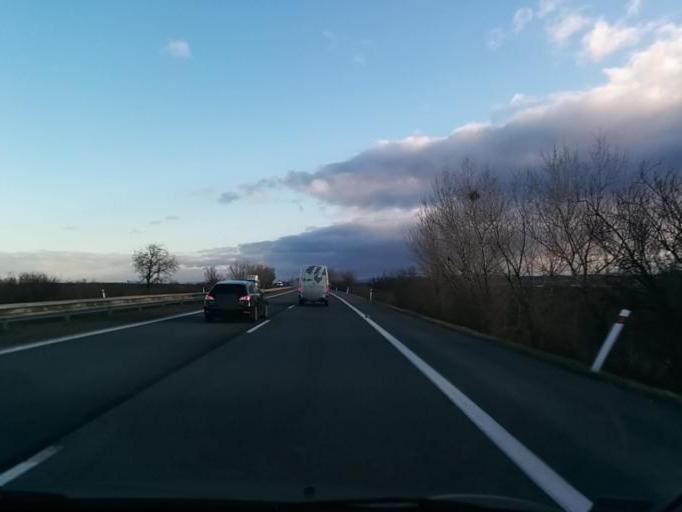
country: SK
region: Trnavsky
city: Leopoldov
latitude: 48.3921
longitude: 17.7437
